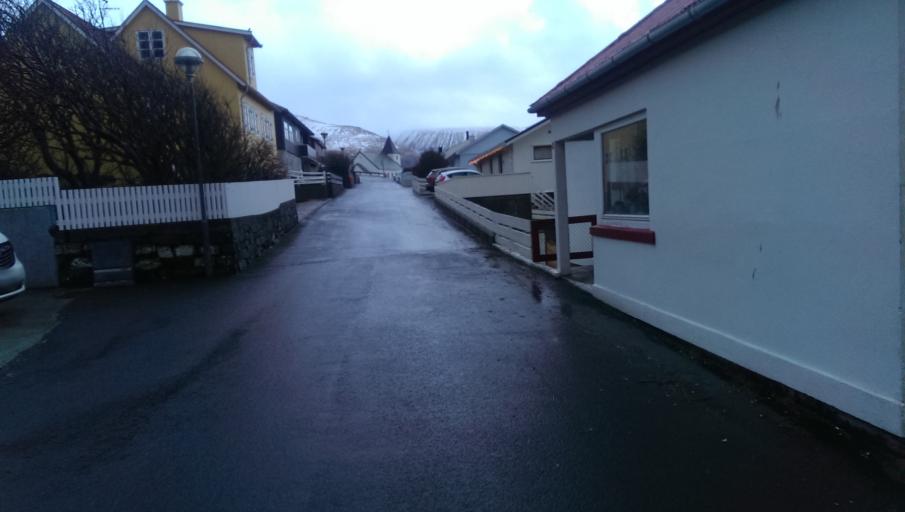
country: FO
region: Eysturoy
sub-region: Eidi
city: Eidi
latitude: 62.2999
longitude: -7.0876
